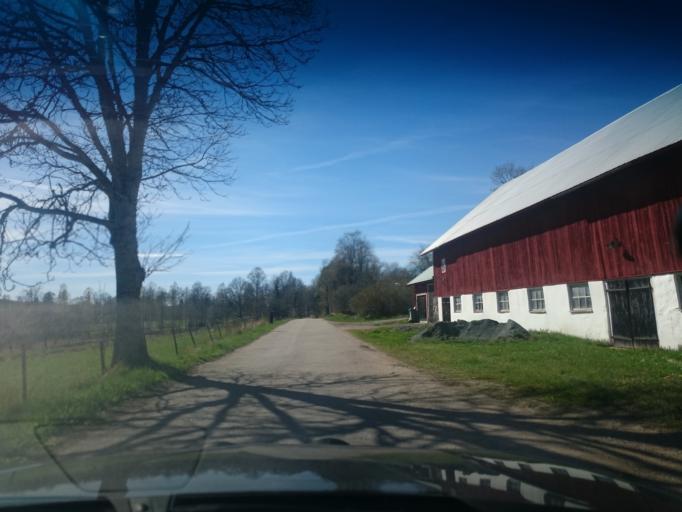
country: SE
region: Kronoberg
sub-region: Uppvidinge Kommun
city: Aseda
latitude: 57.3707
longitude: 15.3845
